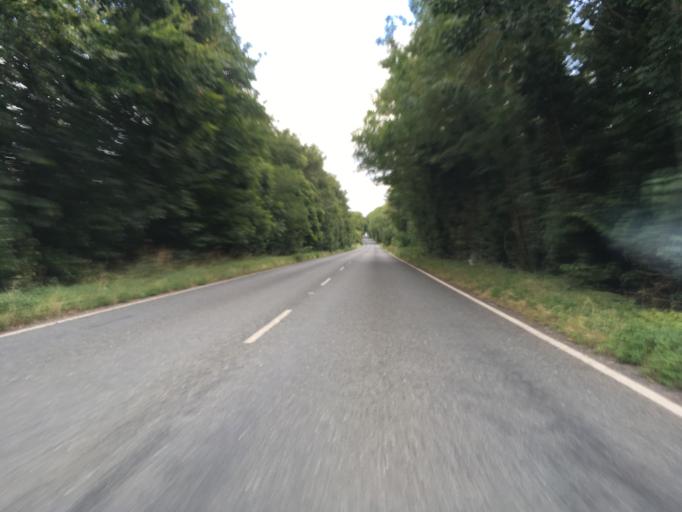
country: GB
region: England
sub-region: Hampshire
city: Kings Worthy
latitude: 51.1114
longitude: -1.2764
